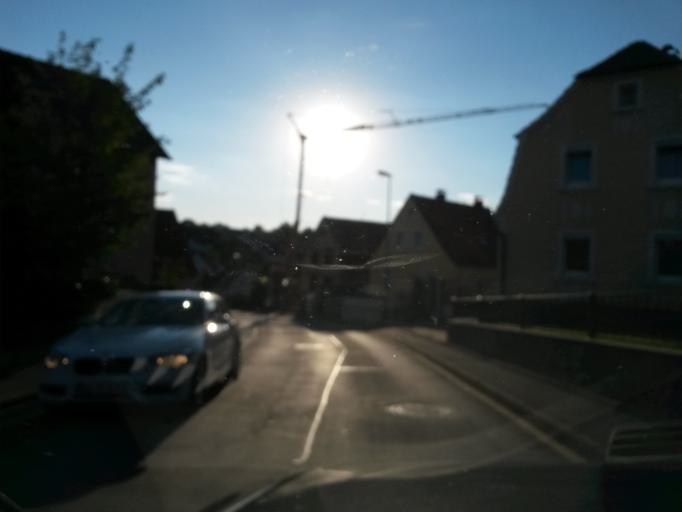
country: DE
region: Bavaria
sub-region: Regierungsbezirk Unterfranken
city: Rimpar
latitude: 49.8523
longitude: 9.9632
